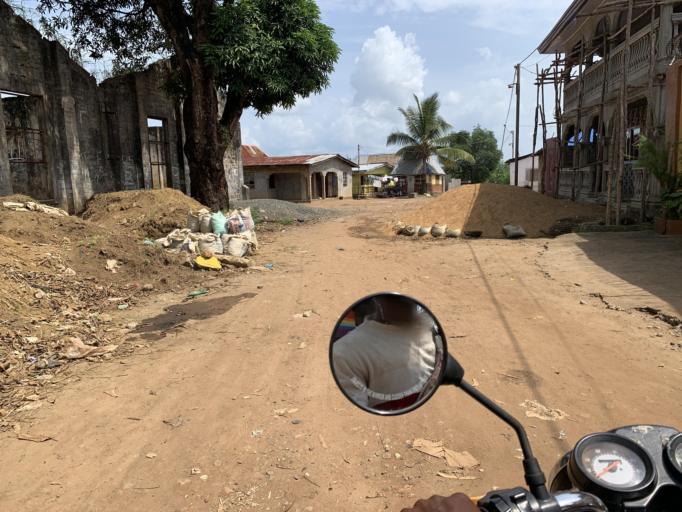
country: SL
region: Western Area
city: Hastings
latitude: 8.4046
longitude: -13.1349
